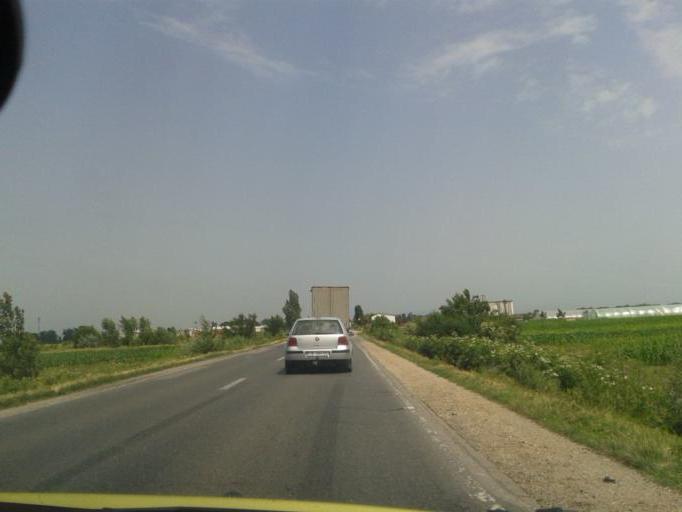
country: RO
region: Dambovita
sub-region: Oras Gaesti
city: Gaesti
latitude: 44.6977
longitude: 25.3116
